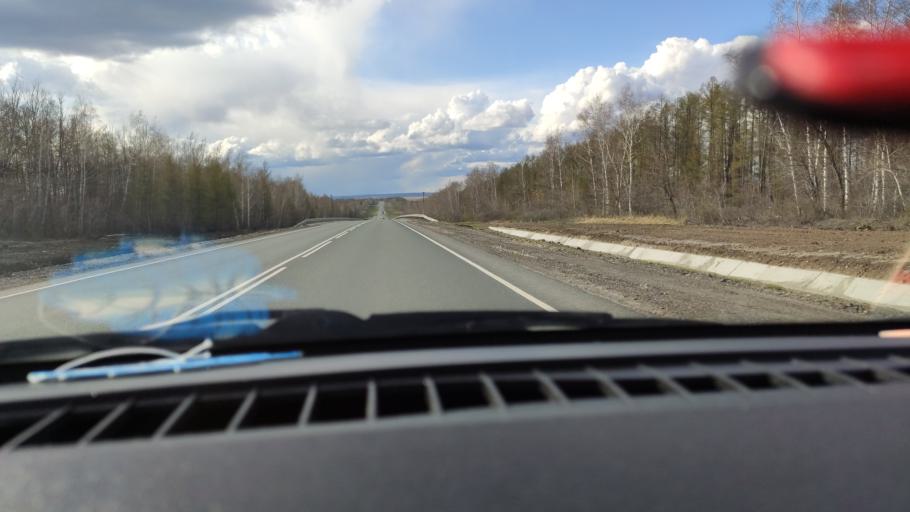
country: RU
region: Saratov
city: Shikhany
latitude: 52.1498
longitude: 47.1903
